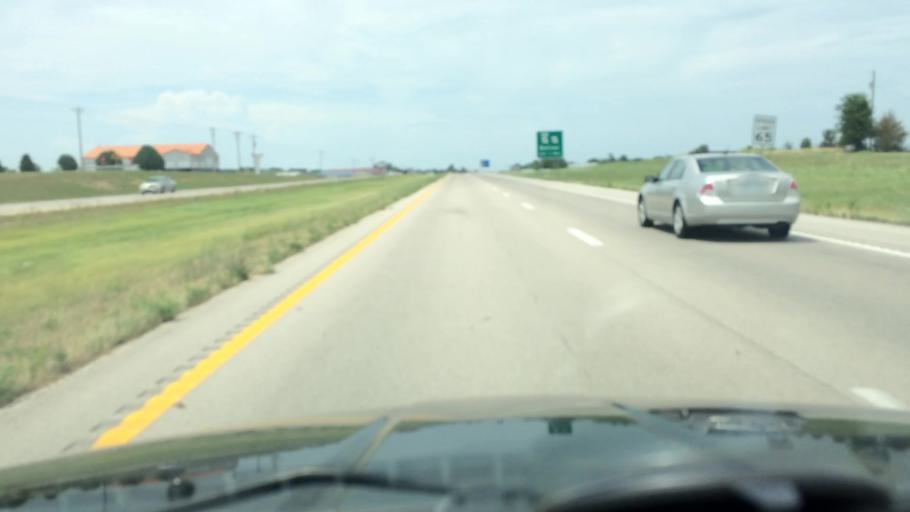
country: US
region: Missouri
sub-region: Polk County
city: Bolivar
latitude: 37.5568
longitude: -93.3893
